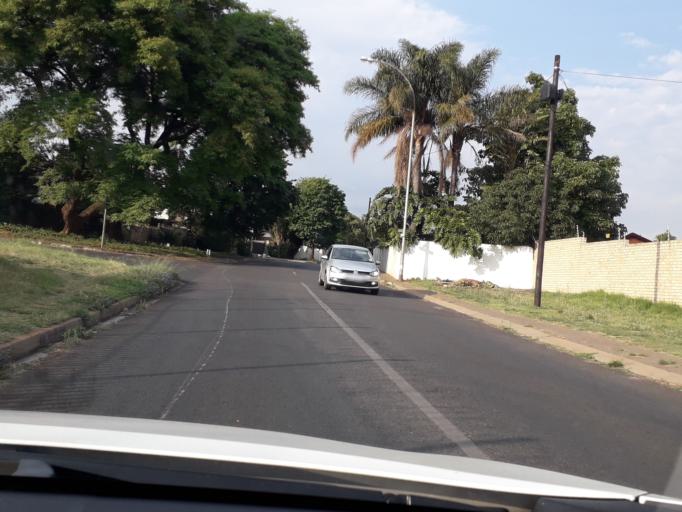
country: ZA
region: Gauteng
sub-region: City of Johannesburg Metropolitan Municipality
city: Johannesburg
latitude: -26.1639
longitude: 27.9810
